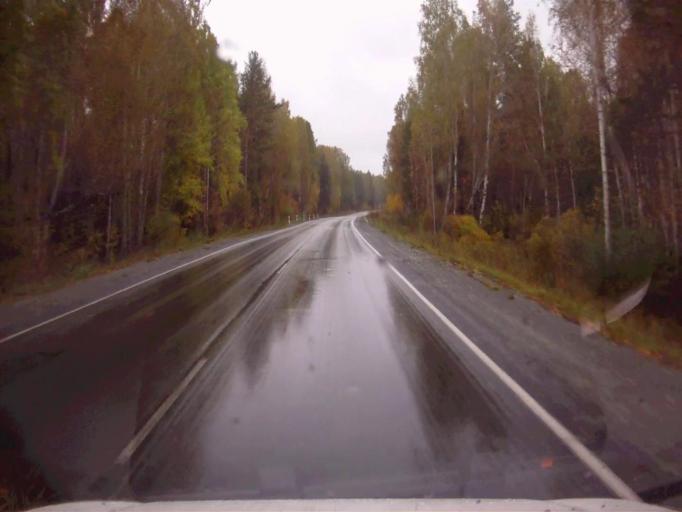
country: RU
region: Chelyabinsk
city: Tayginka
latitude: 55.5980
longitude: 60.6167
